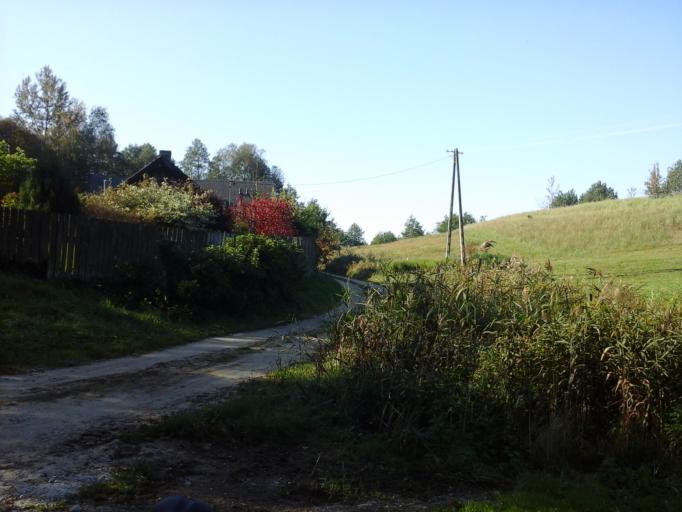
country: PL
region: Kujawsko-Pomorskie
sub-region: Powiat brodnicki
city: Gorzno
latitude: 53.2150
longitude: 19.6575
